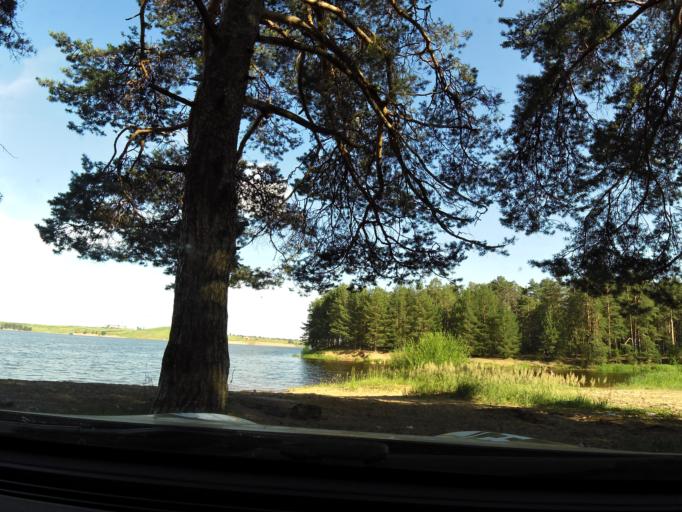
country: RU
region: Kirov
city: Belaya Kholunitsa
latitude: 58.8608
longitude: 50.8438
